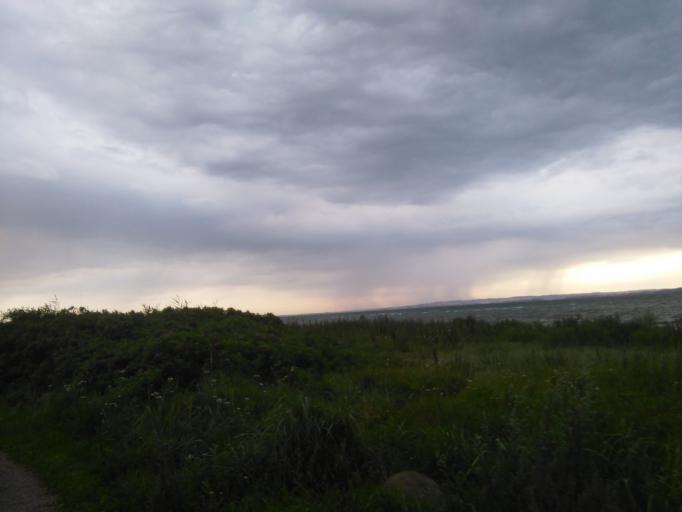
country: DK
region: Central Jutland
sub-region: Arhus Kommune
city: Hjortshoj
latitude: 56.2159
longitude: 10.2930
